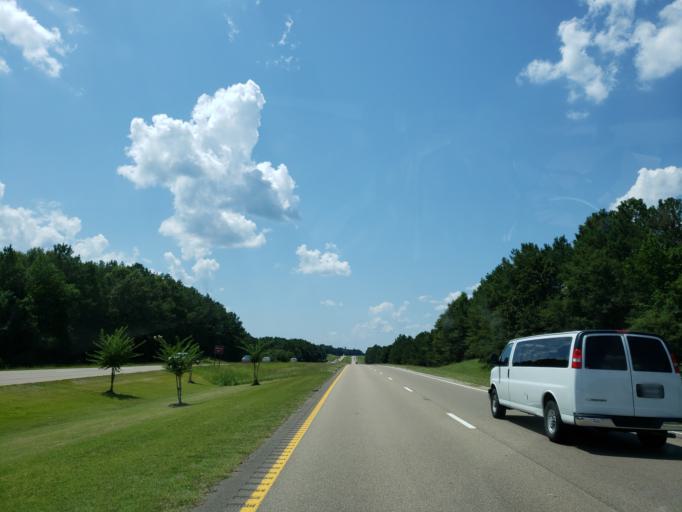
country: US
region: Mississippi
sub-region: Perry County
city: New Augusta
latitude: 31.1616
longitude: -88.9266
